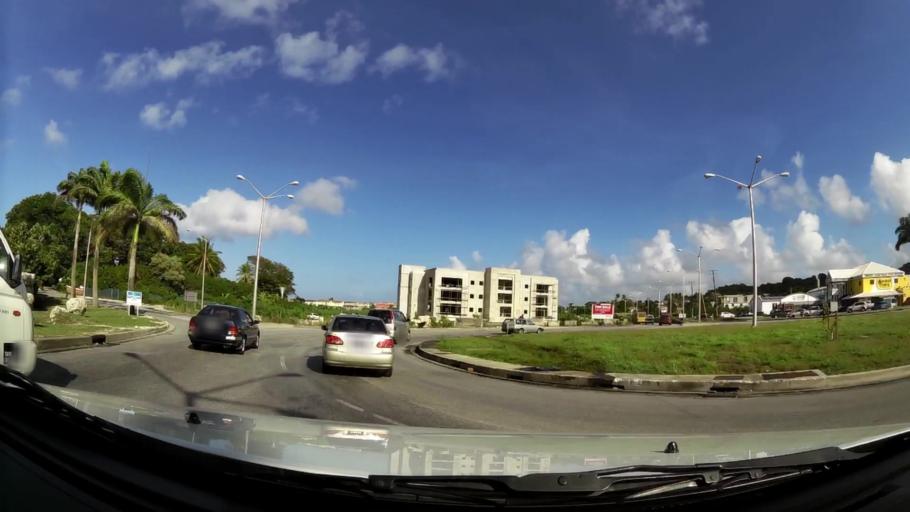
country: BB
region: Saint James
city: Holetown
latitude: 13.1537
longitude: -59.6132
